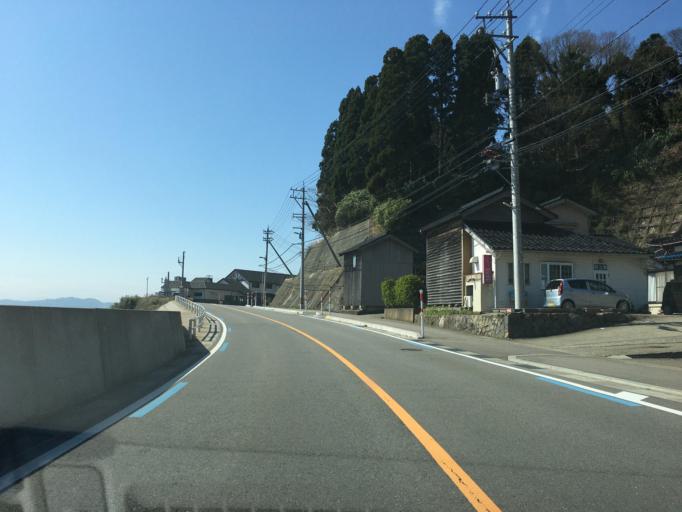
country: JP
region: Toyama
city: Himi
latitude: 36.9009
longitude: 137.0115
